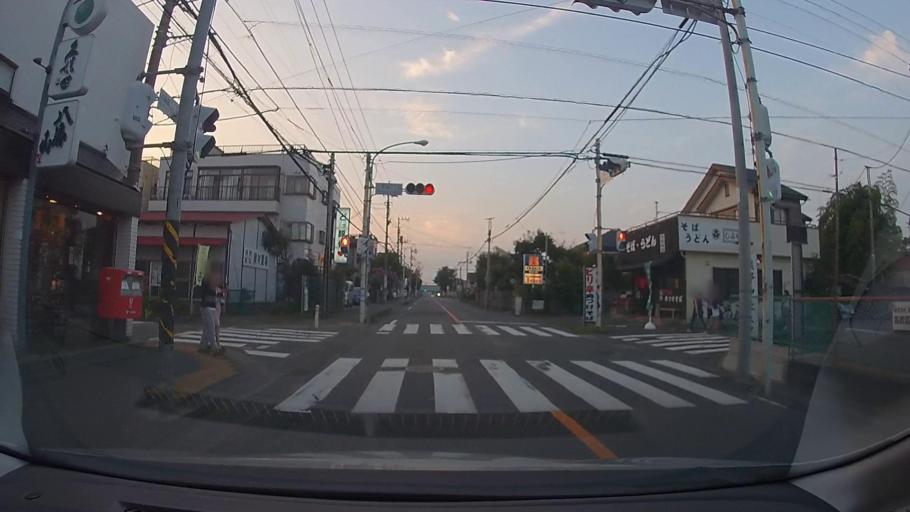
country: JP
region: Kanagawa
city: Minami-rinkan
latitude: 35.4759
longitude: 139.4547
